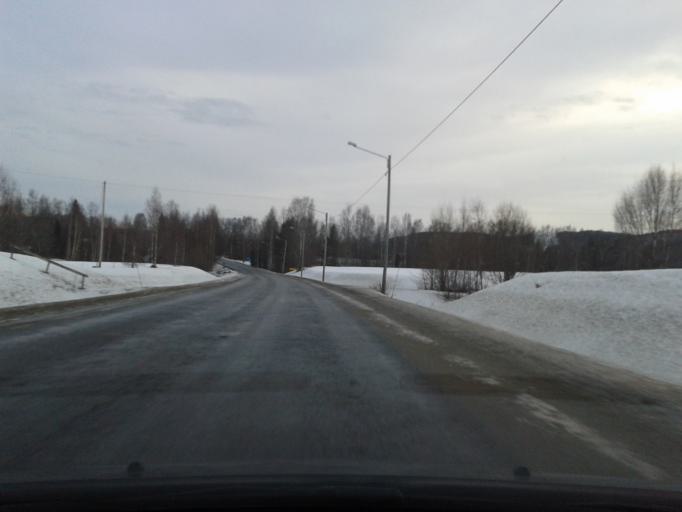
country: SE
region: Vaesternorrland
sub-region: Solleftea Kommun
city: Solleftea
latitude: 63.2440
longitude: 17.2075
